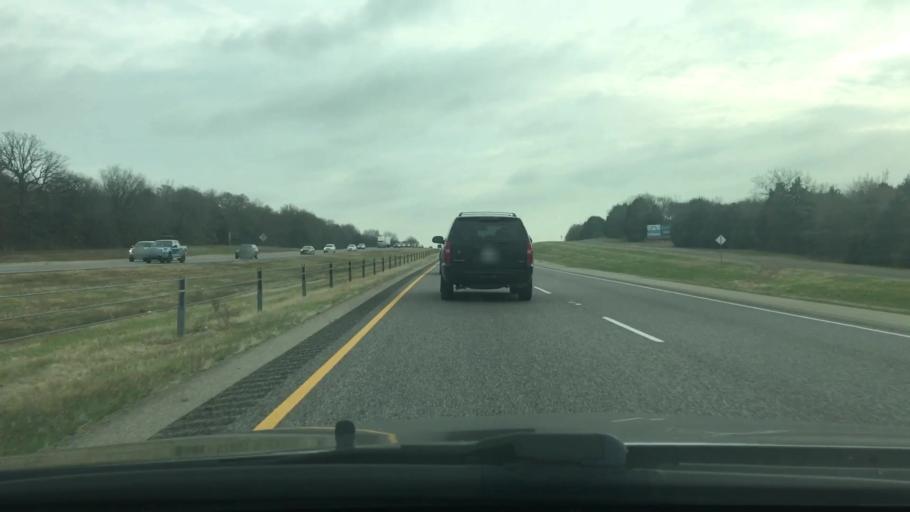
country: US
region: Texas
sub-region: Freestone County
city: Fairfield
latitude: 31.6444
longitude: -96.1592
